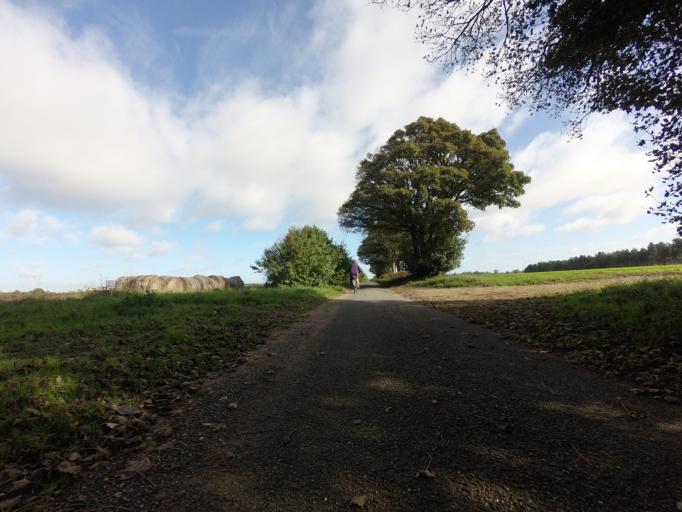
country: GB
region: England
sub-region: Norfolk
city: Dersingham
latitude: 52.8691
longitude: 0.6685
